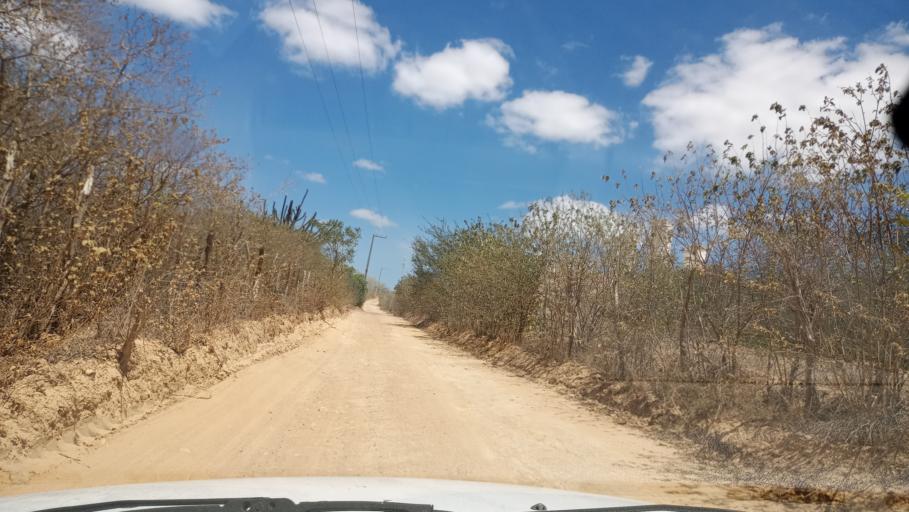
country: BR
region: Rio Grande do Norte
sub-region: Sao Paulo Do Potengi
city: Sao Paulo do Potengi
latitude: -5.7920
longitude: -35.9195
